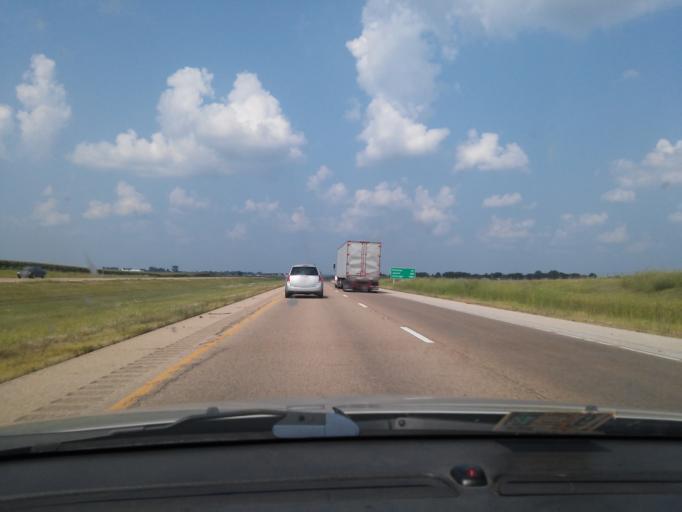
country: US
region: Illinois
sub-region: McLean County
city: Chenoa
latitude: 40.7531
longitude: -88.7323
